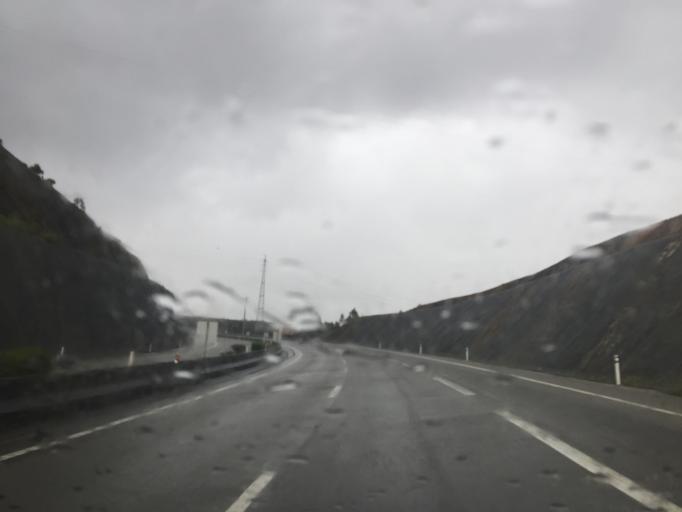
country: PT
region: Aveiro
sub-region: Sever do Vouga
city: Sever do Vouga
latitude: 40.6500
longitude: -8.3720
